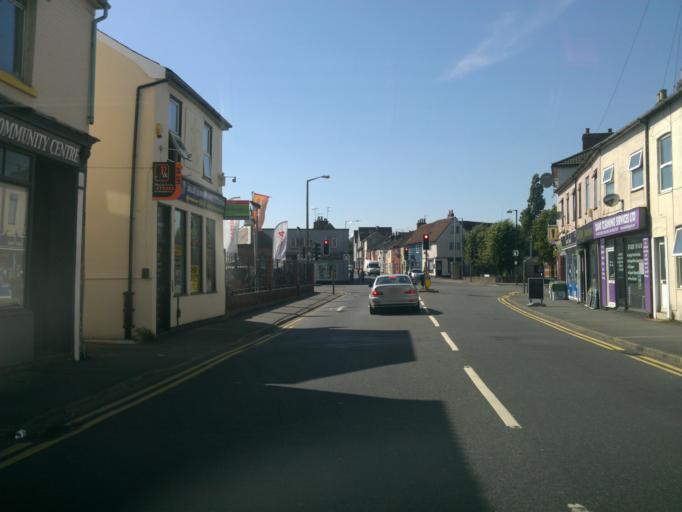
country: GB
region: England
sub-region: Essex
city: Colchester
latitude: 51.8852
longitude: 0.9146
